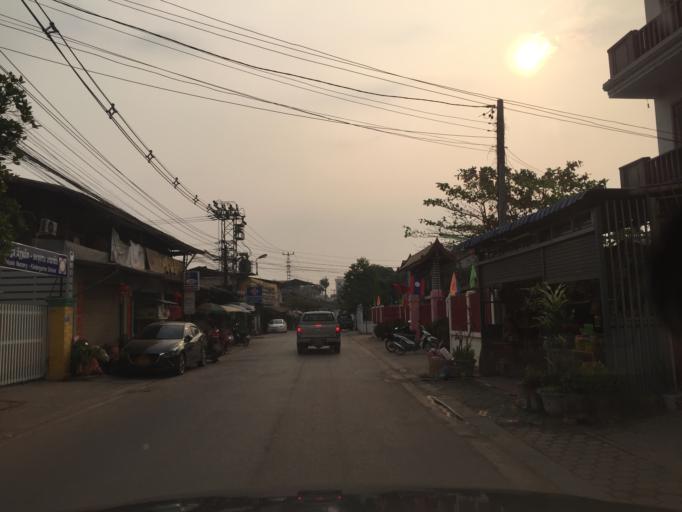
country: LA
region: Vientiane
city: Vientiane
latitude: 17.9746
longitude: 102.6112
